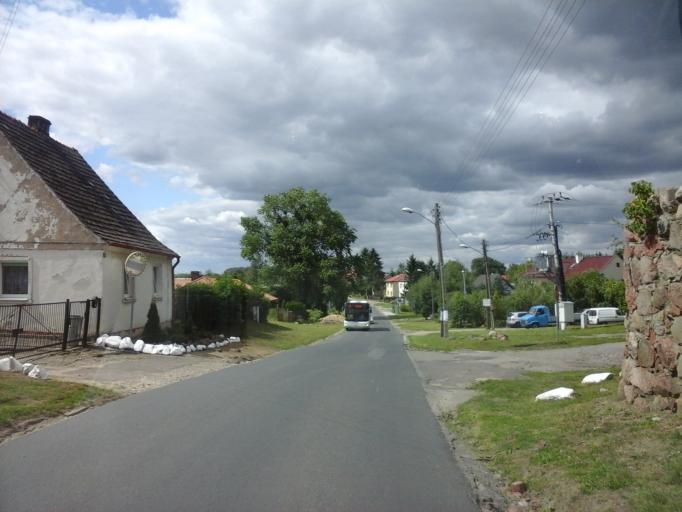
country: PL
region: West Pomeranian Voivodeship
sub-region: Powiat policki
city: Przeclaw
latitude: 53.4133
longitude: 14.4290
